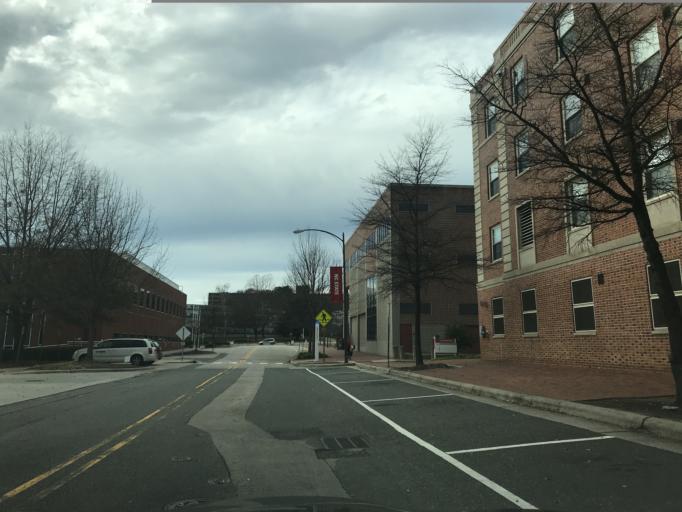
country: US
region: North Carolina
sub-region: Wake County
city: West Raleigh
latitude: 35.7846
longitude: -78.6741
